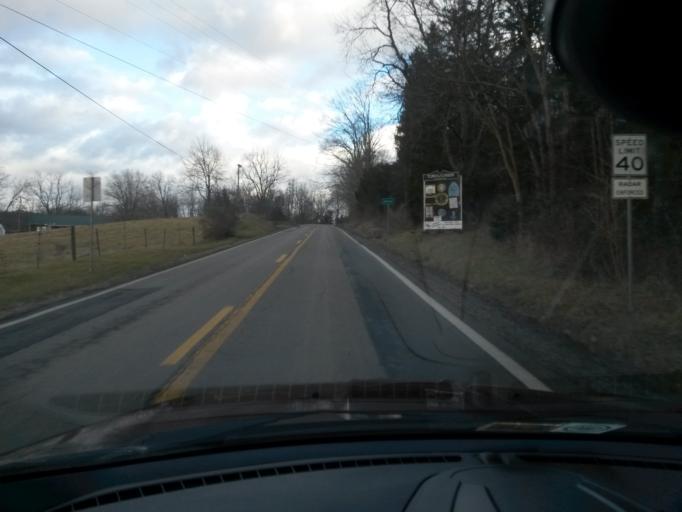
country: US
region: West Virginia
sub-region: Monroe County
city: Union
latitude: 37.5865
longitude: -80.5497
